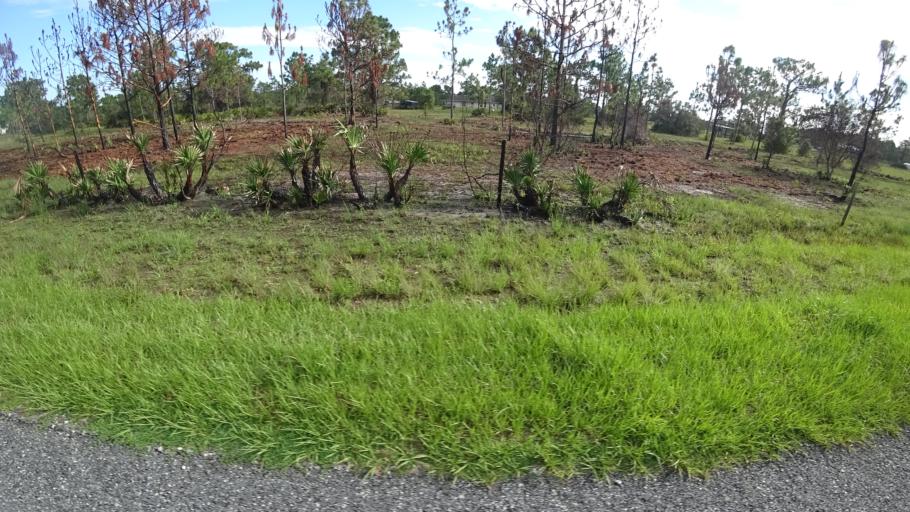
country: US
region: Florida
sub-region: Sarasota County
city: Fruitville
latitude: 27.4088
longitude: -82.2844
